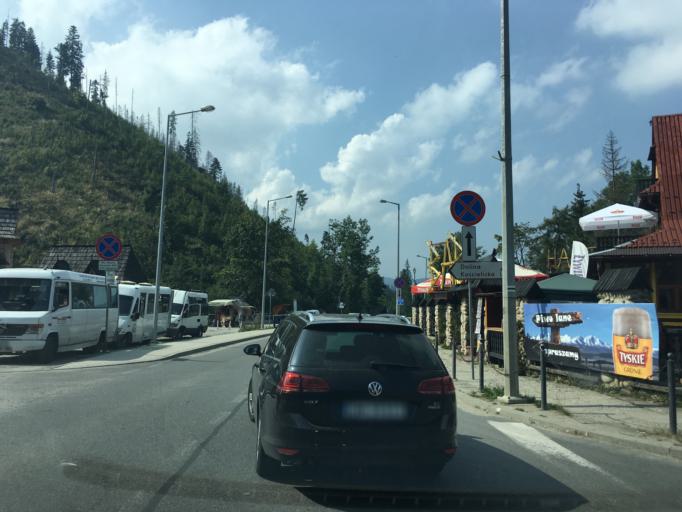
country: PL
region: Lesser Poland Voivodeship
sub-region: Powiat tatrzanski
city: Koscielisko
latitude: 49.2755
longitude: 19.8690
